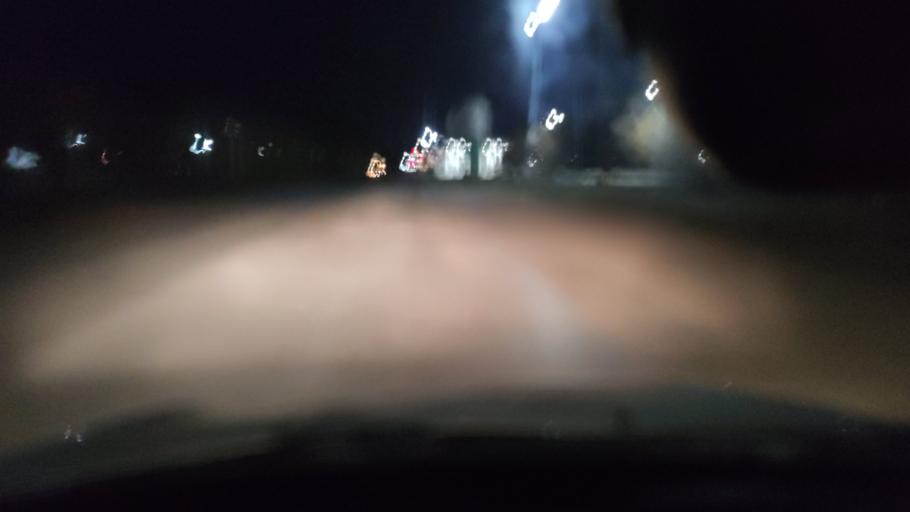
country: RU
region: Samara
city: Podstepki
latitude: 53.5709
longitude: 49.0872
